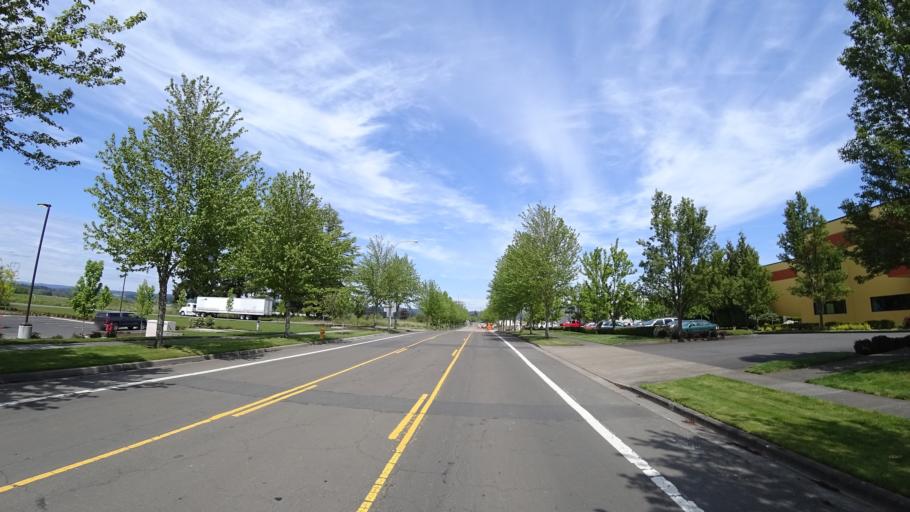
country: US
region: Oregon
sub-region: Washington County
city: Rockcreek
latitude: 45.5709
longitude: -122.9086
